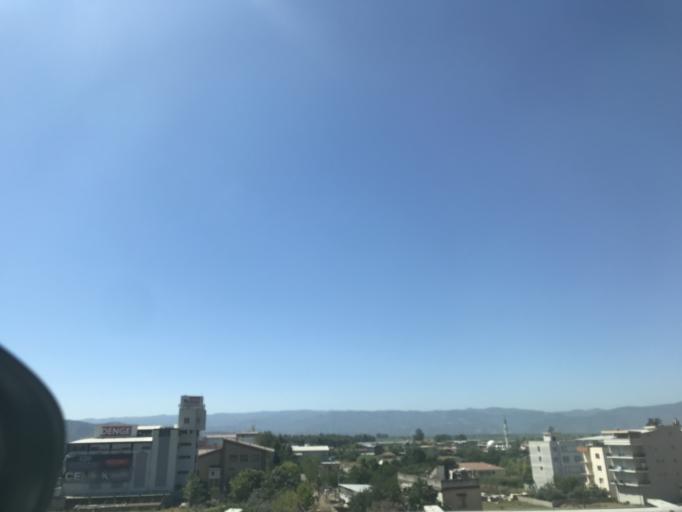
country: TR
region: Aydin
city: Aydin
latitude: 37.8205
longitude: 27.8383
